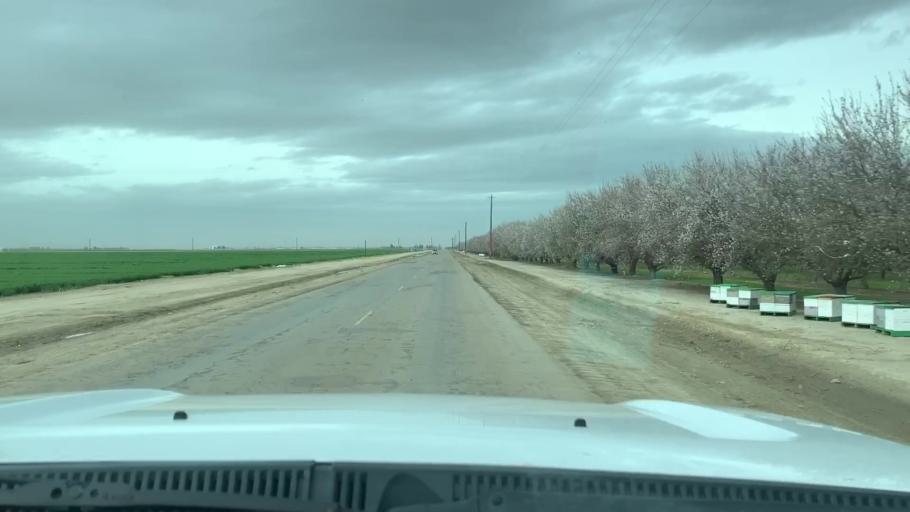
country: US
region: California
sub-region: Kern County
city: Wasco
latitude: 35.5661
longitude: -119.4028
